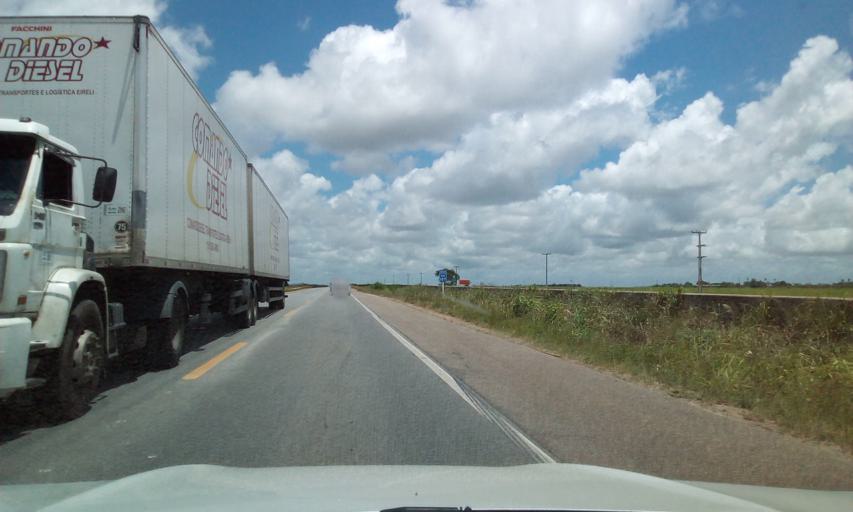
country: BR
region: Alagoas
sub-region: Sao Miguel Dos Campos
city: Sao Miguel dos Campos
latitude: -9.8964
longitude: -36.2021
